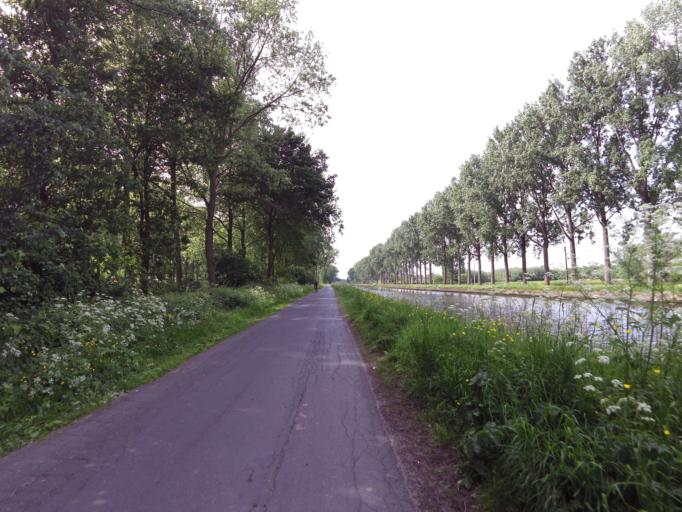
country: BE
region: Flanders
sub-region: Provincie West-Vlaanderen
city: Oostkamp
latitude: 51.1634
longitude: 3.2559
